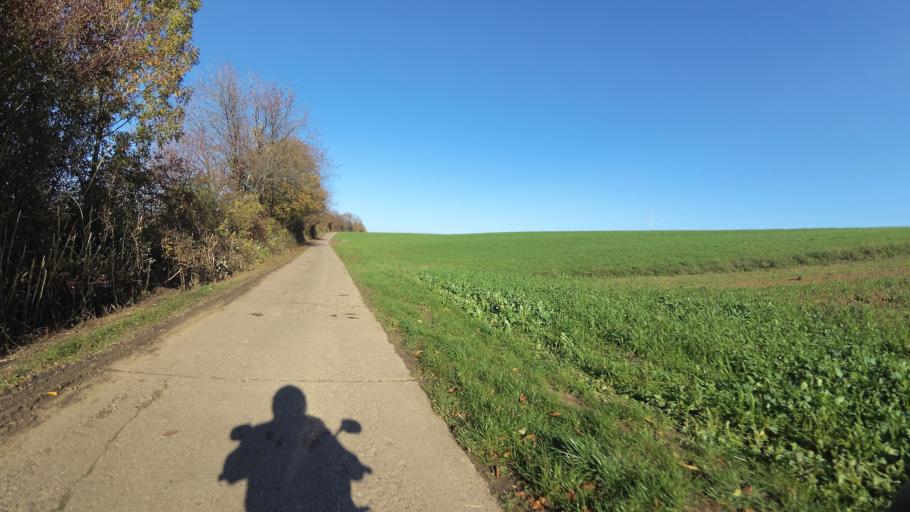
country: DE
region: Saarland
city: Losheim
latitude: 49.4748
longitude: 6.7416
